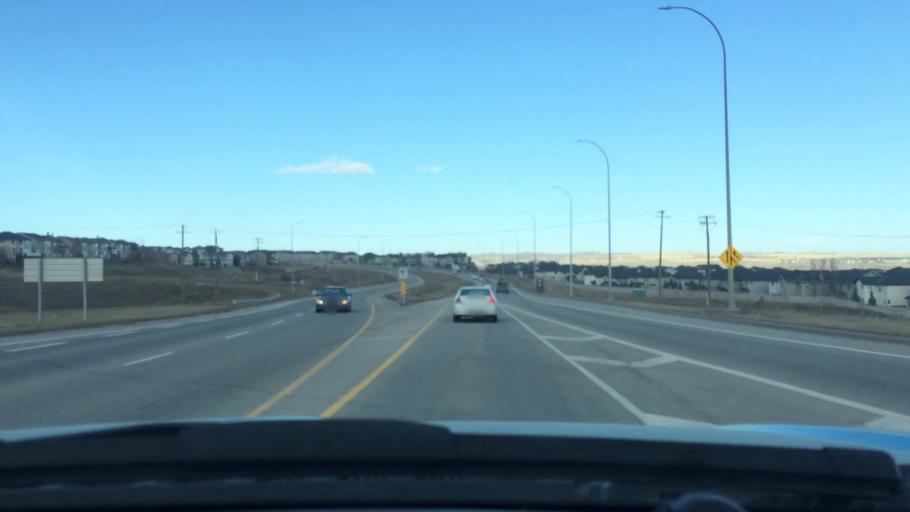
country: CA
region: Alberta
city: Calgary
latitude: 51.1564
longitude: -114.1410
